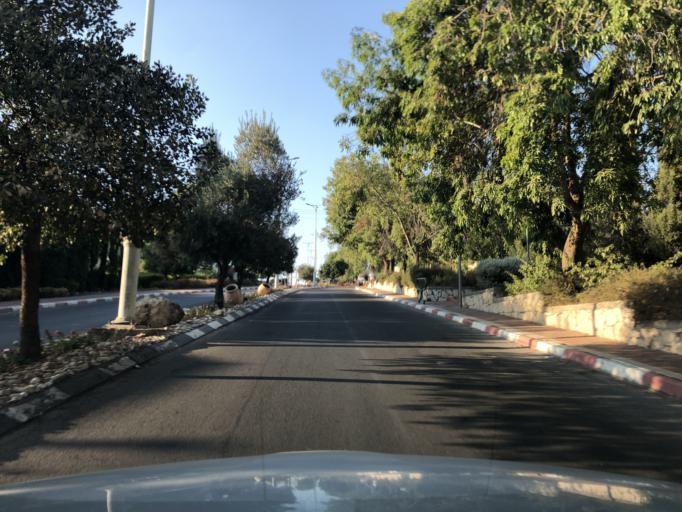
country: PS
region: West Bank
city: Hablah
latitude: 32.1512
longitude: 34.9712
